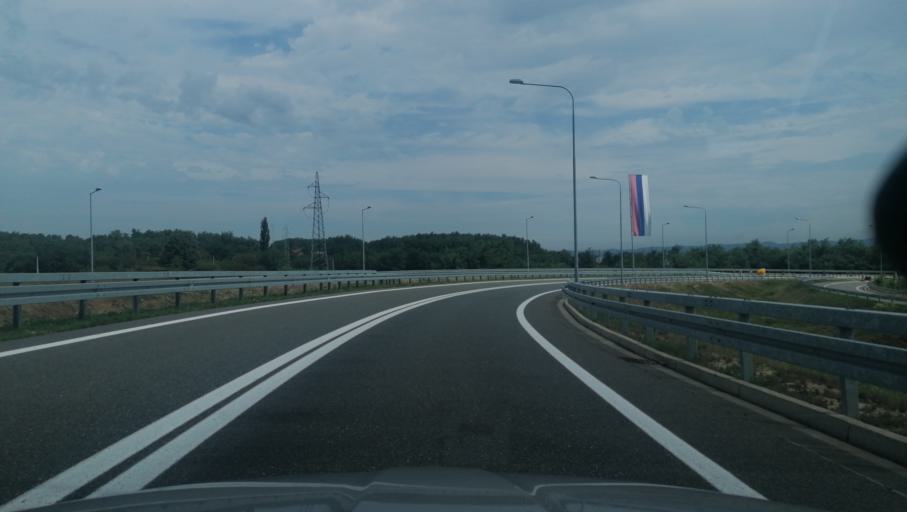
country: BA
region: Republika Srpska
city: Doboj
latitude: 44.8107
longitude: 18.0418
